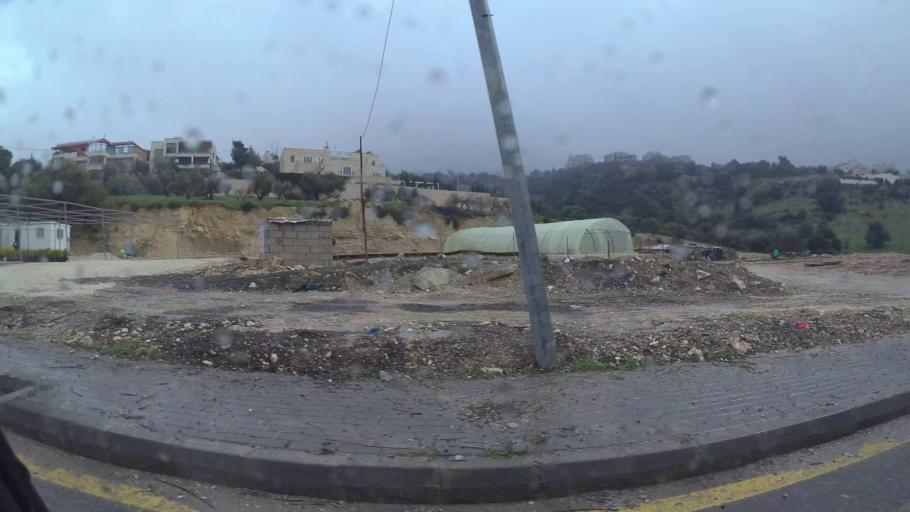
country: JO
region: Amman
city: Wadi as Sir
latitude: 32.0094
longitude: 35.7918
